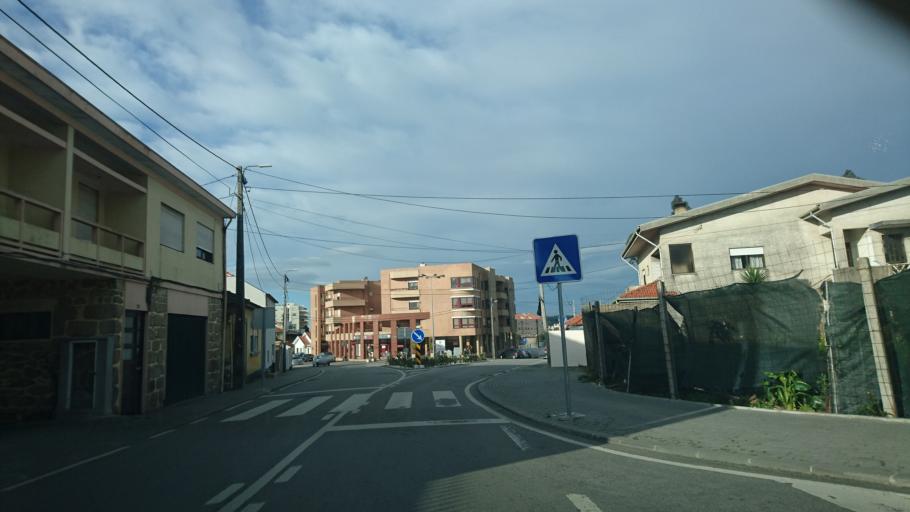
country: PT
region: Aveiro
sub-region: Santa Maria da Feira
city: Pacos de Brandao
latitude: 40.9735
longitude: -8.5791
